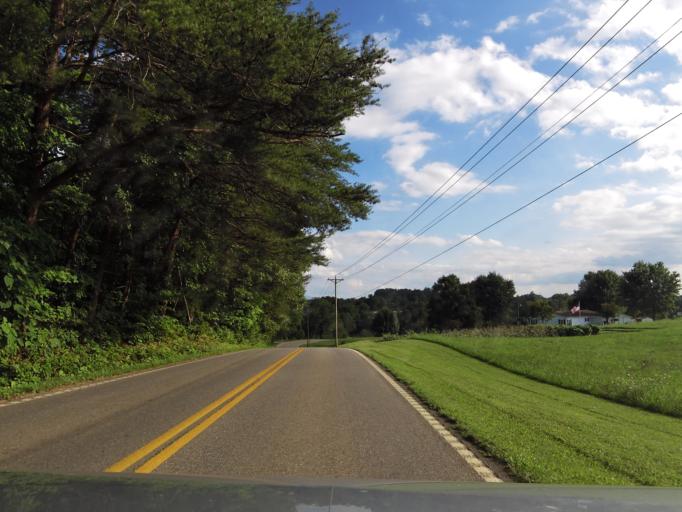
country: US
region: Tennessee
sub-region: Loudon County
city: Greenback
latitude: 35.6337
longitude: -84.0994
